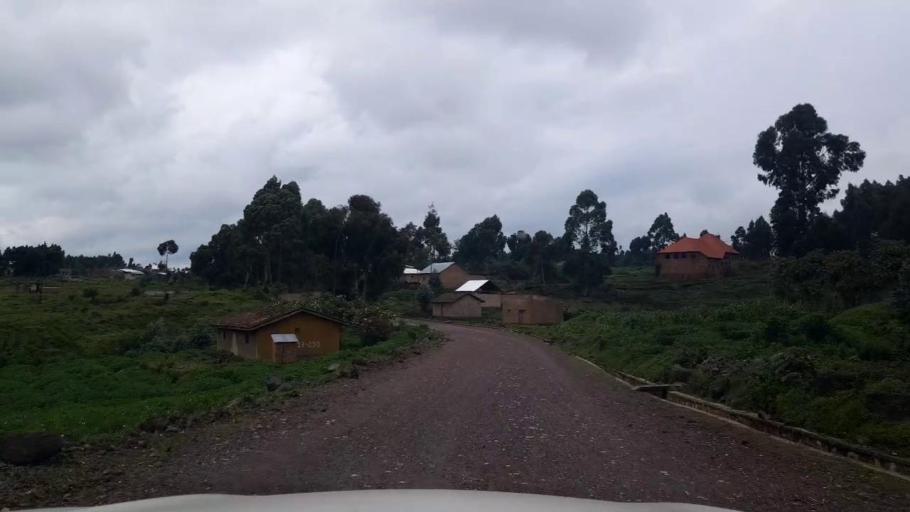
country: RW
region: Northern Province
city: Musanze
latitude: -1.5881
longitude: 29.4713
